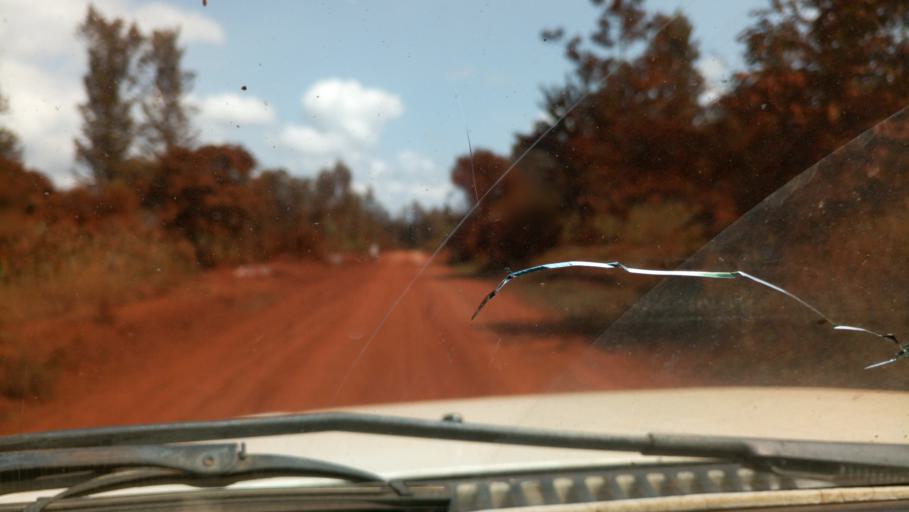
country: KE
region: Murang'a District
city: Karuri
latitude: -0.7571
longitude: 37.2161
